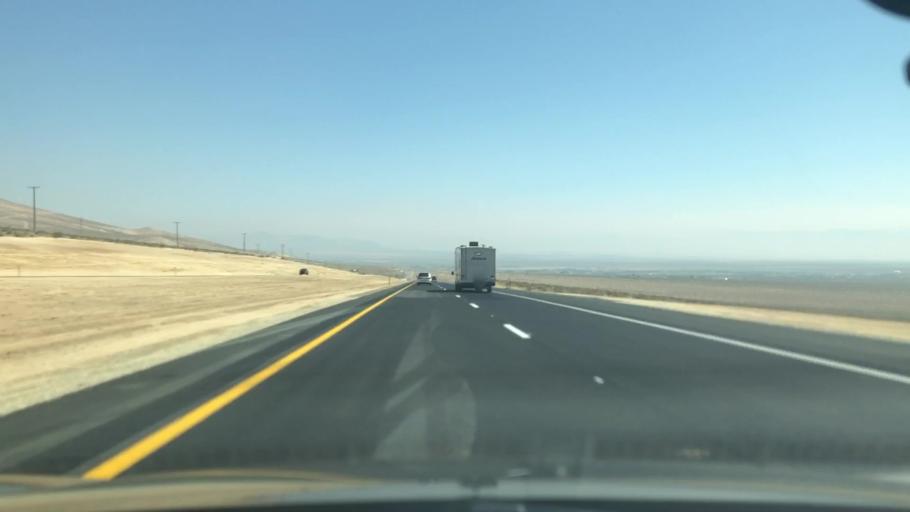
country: US
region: California
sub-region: Kern County
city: Inyokern
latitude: 35.6501
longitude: -117.8786
